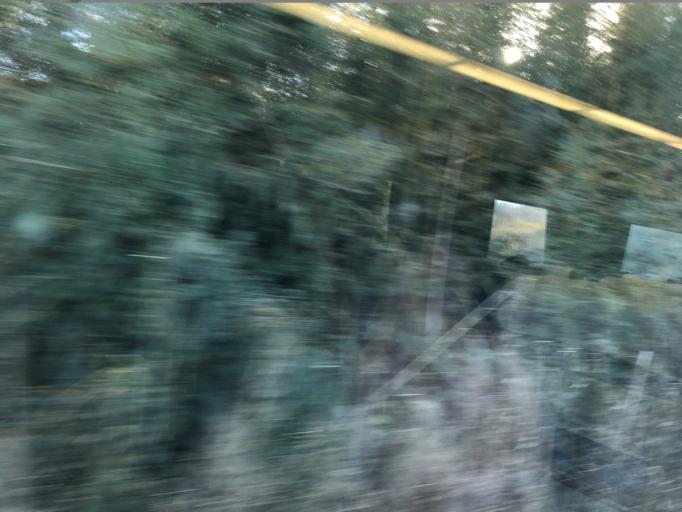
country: JP
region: Kochi
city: Nakamura
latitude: 33.0397
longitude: 133.0358
